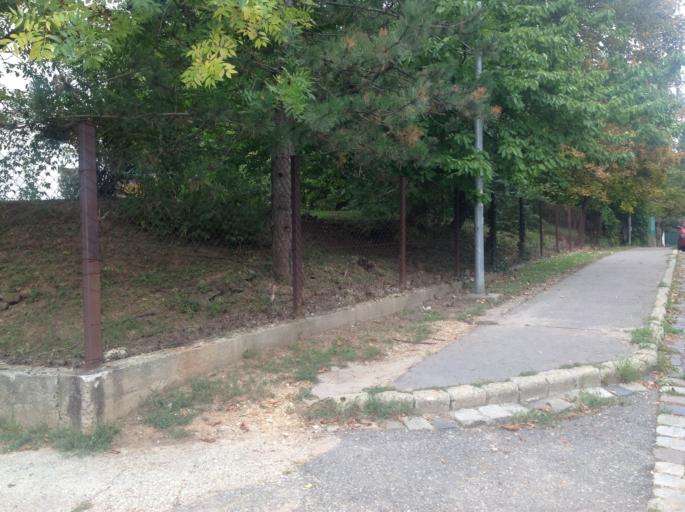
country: HU
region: Pest
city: Budaors
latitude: 47.5000
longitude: 18.9742
